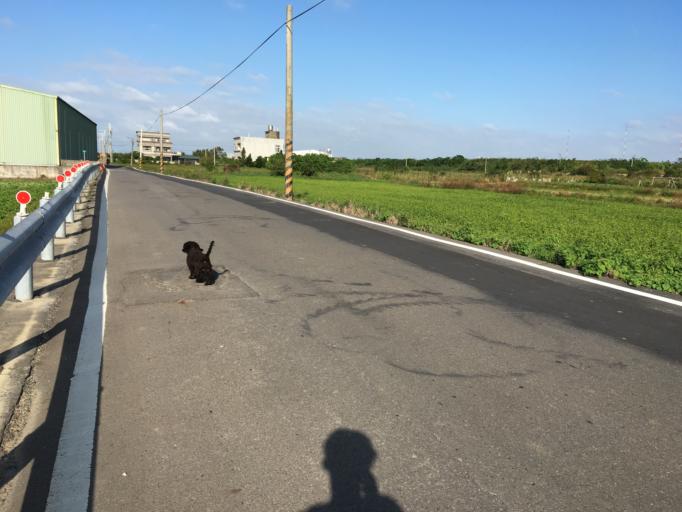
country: TW
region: Taiwan
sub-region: Hsinchu
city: Zhubei
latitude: 24.9275
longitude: 120.9853
